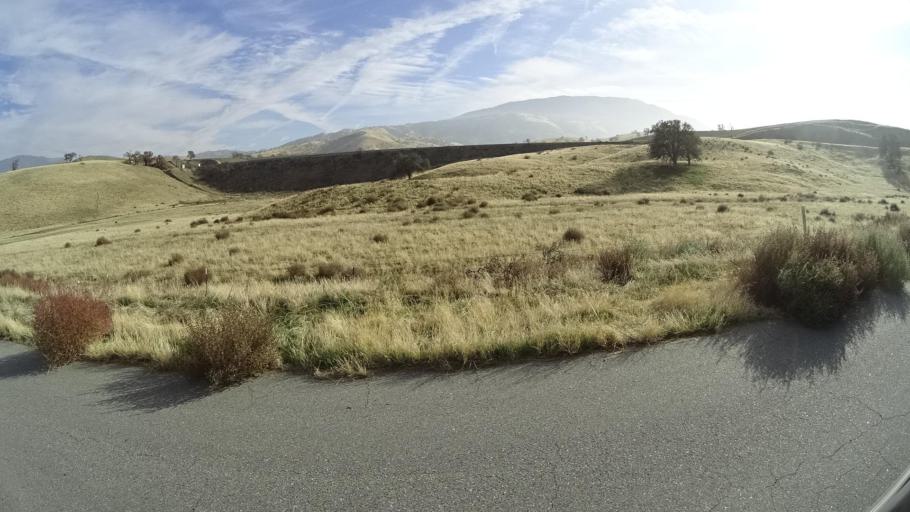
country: US
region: California
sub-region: Kern County
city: Bear Valley Springs
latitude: 35.2881
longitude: -118.6494
